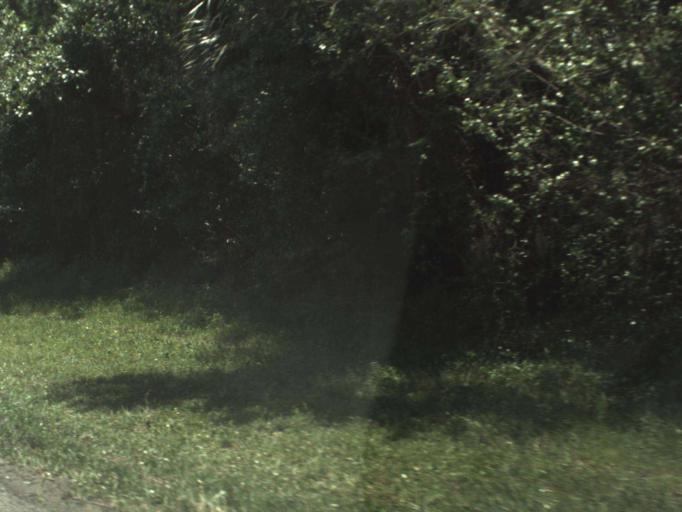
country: US
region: Florida
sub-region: Volusia County
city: Ponce Inlet
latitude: 29.1005
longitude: -80.9708
